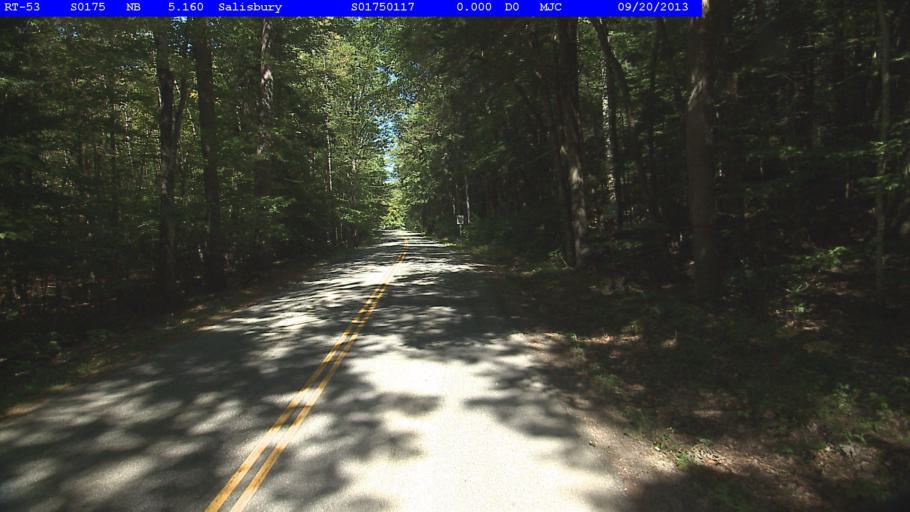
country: US
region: Vermont
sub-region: Rutland County
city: Brandon
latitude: 43.8977
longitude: -73.0639
